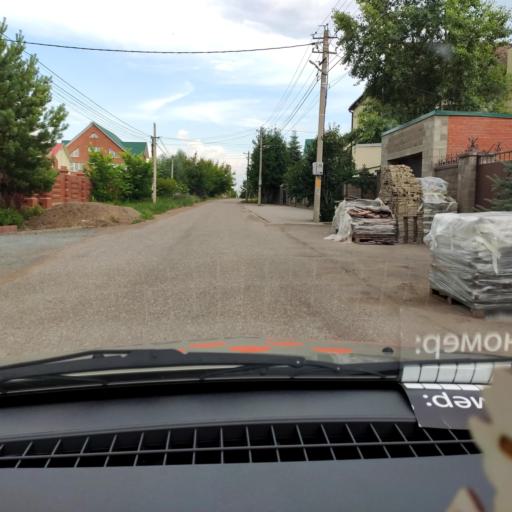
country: RU
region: Bashkortostan
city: Ufa
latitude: 54.6200
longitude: 55.9171
